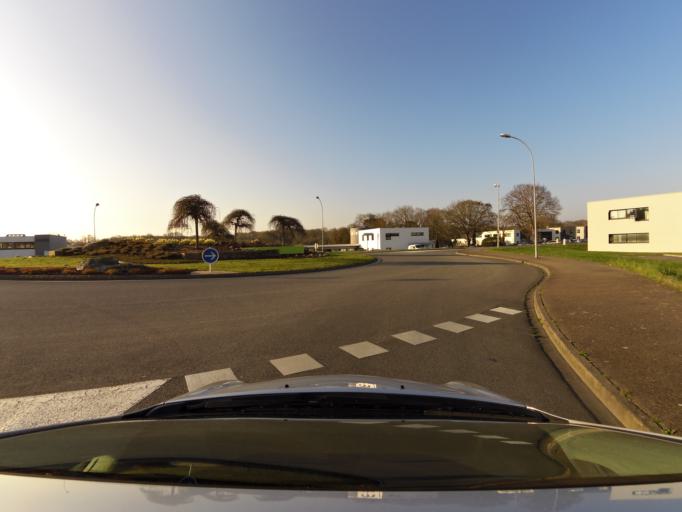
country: FR
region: Brittany
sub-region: Departement du Morbihan
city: Larmor-Plage
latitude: 47.7251
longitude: -3.3863
